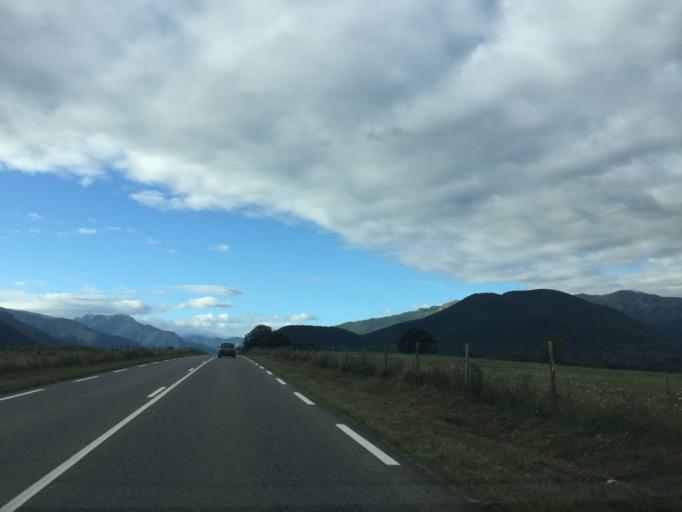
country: FR
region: Midi-Pyrenees
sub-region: Departement des Hautes-Pyrenees
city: La Barthe-de-Neste
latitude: 43.0541
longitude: 0.3611
